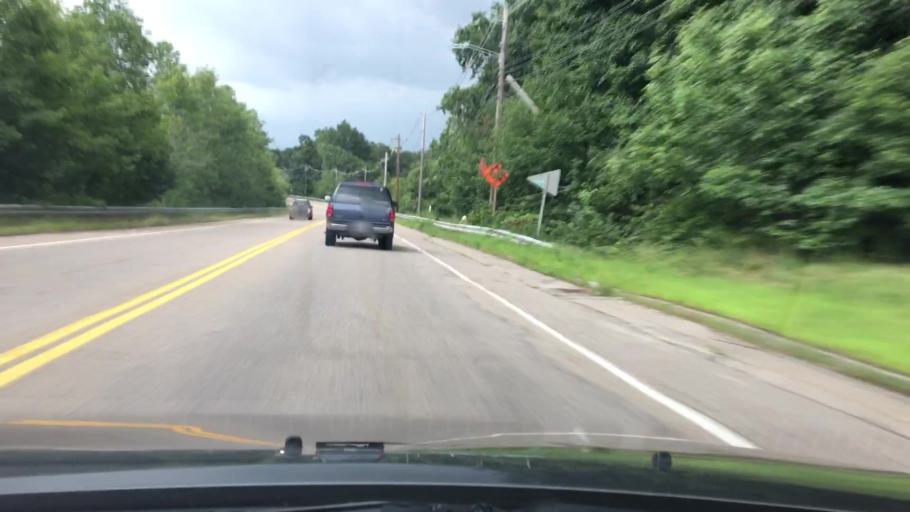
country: US
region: Massachusetts
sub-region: Norfolk County
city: Plainville
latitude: 41.9669
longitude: -71.3468
